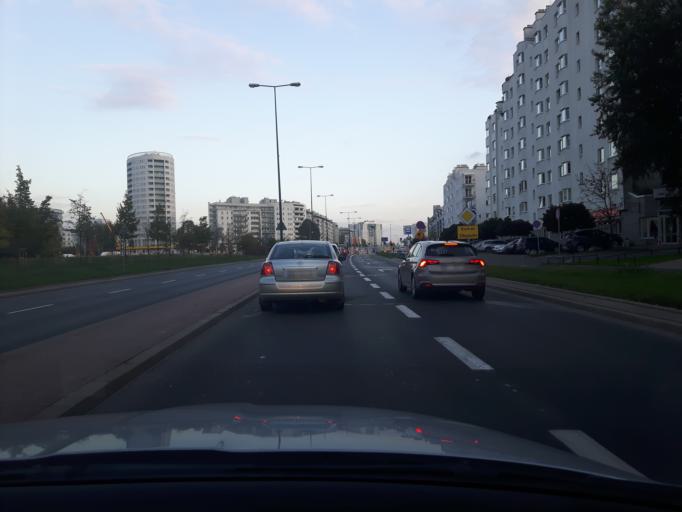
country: PL
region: Masovian Voivodeship
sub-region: Warszawa
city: Ursynow
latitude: 52.1470
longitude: 21.0498
